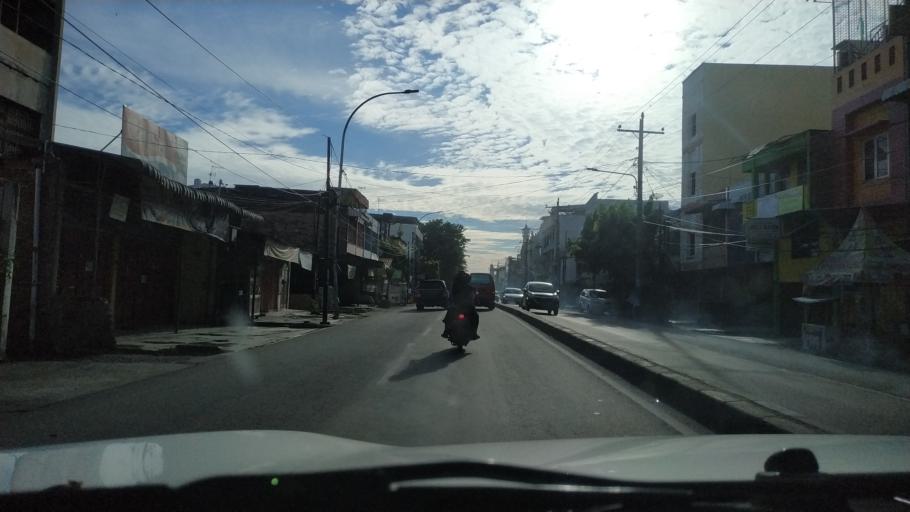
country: ID
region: North Sumatra
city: Medan
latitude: 3.5984
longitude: 98.6974
